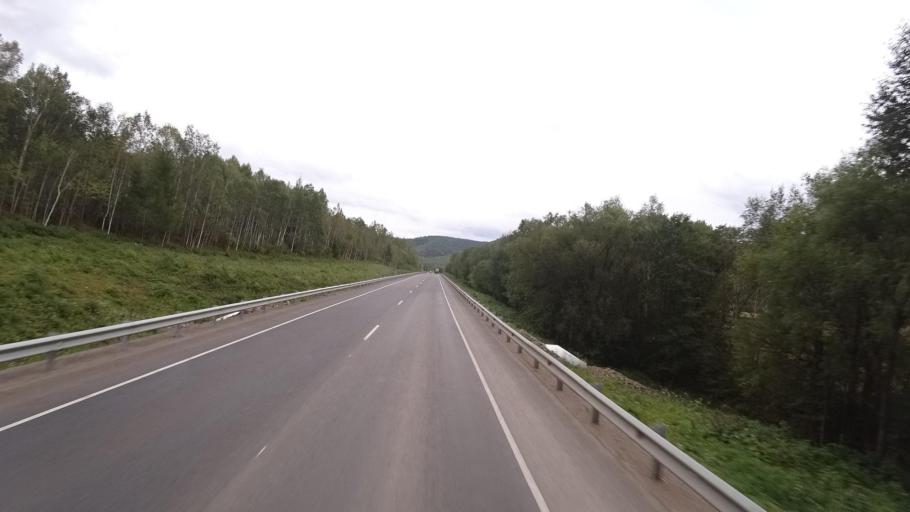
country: RU
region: Jewish Autonomous Oblast
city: Khingansk
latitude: 48.9851
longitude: 131.1416
